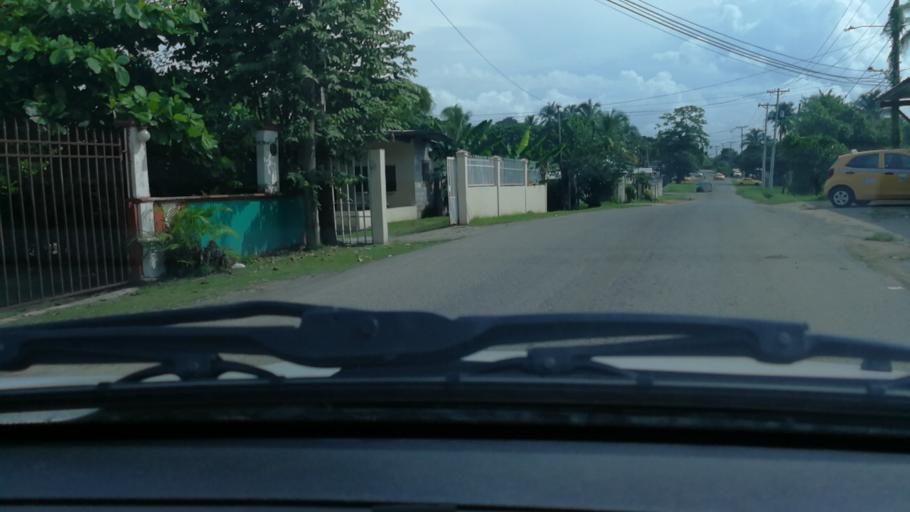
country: PA
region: Panama
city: Pacora
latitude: 9.0793
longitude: -79.2947
